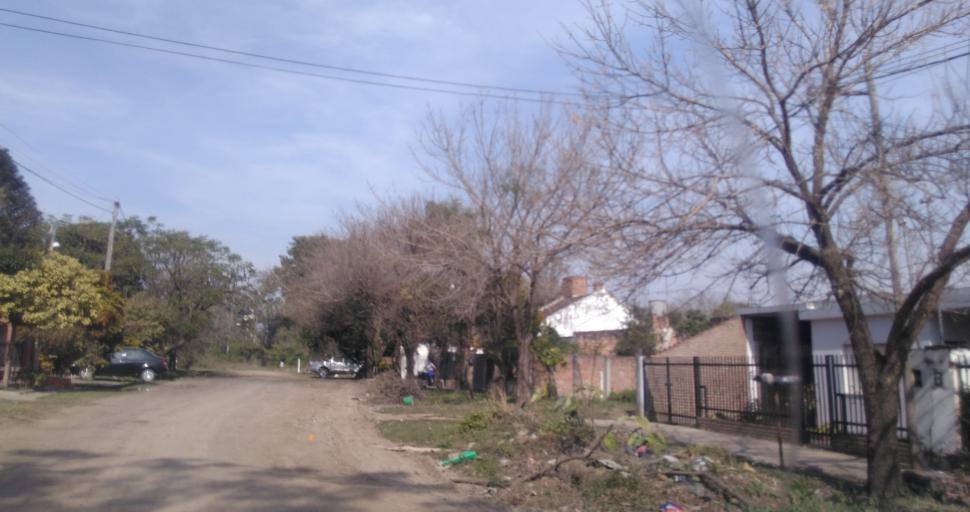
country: AR
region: Chaco
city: Fontana
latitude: -27.4288
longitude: -59.0150
